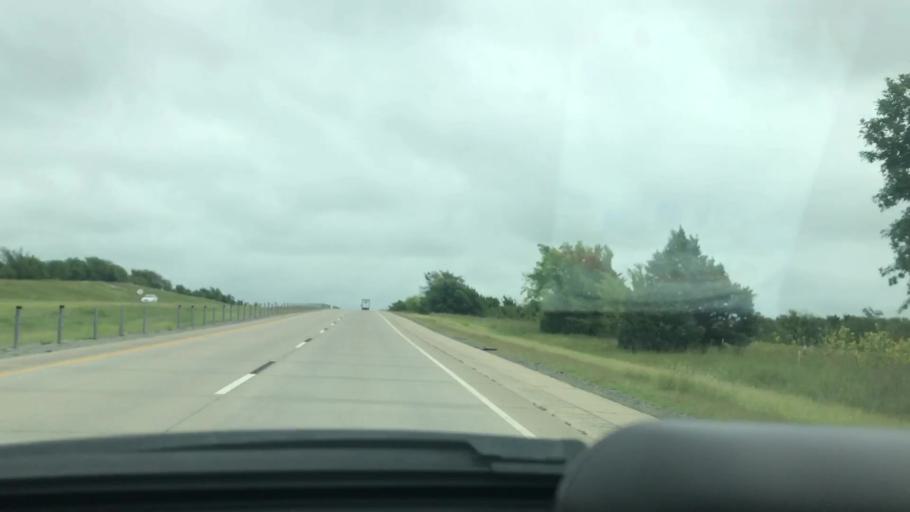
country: US
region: Oklahoma
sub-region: Pittsburg County
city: McAlester
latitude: 34.6824
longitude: -95.9284
